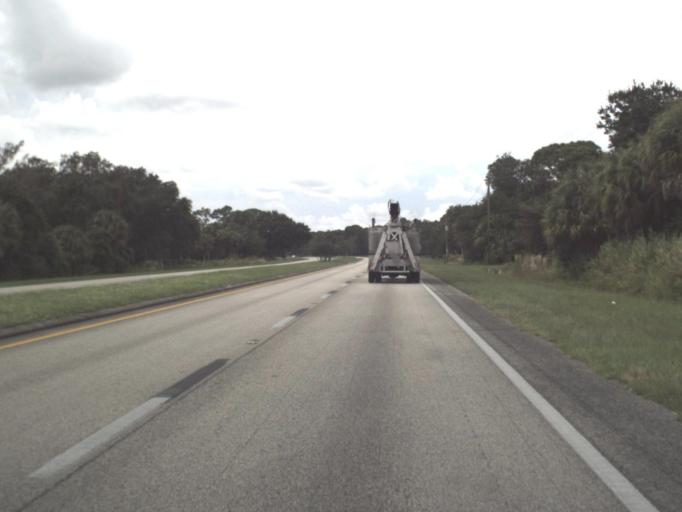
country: US
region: Florida
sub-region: Lee County
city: Olga
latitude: 26.7154
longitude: -81.6905
